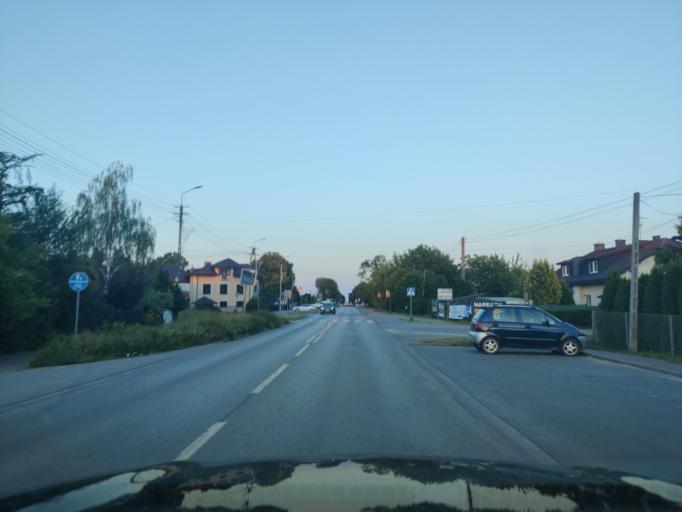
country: PL
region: Masovian Voivodeship
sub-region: Powiat nowodworski
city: Nowy Dwor Mazowiecki
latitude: 52.3914
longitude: 20.7293
